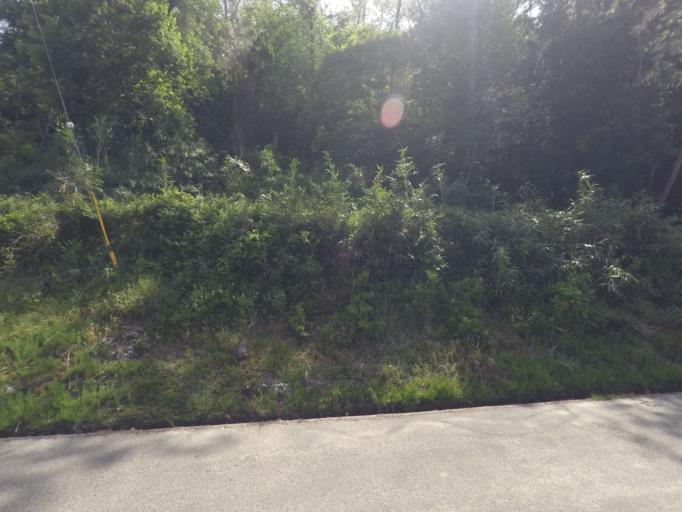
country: JP
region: Ibaraki
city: Makabe
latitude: 36.2596
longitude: 140.1044
